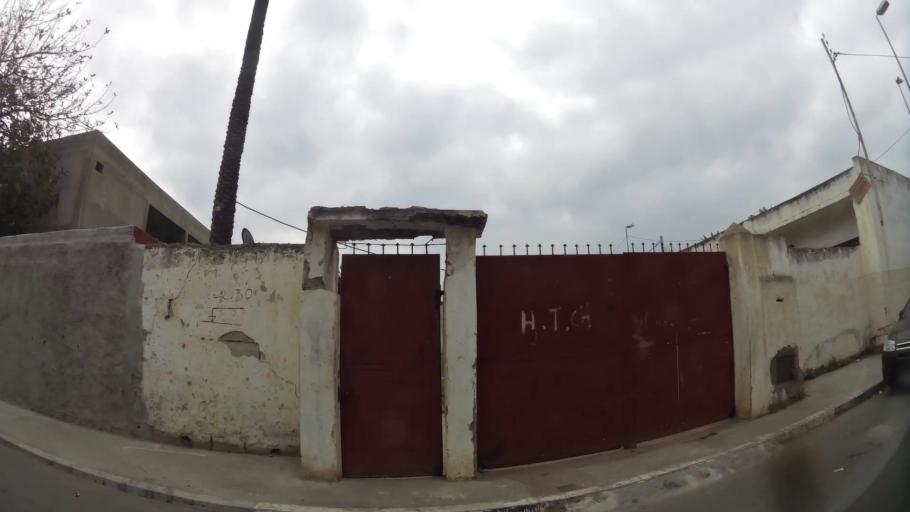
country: MA
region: Rabat-Sale-Zemmour-Zaer
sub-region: Rabat
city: Rabat
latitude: 34.0023
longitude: -6.8711
